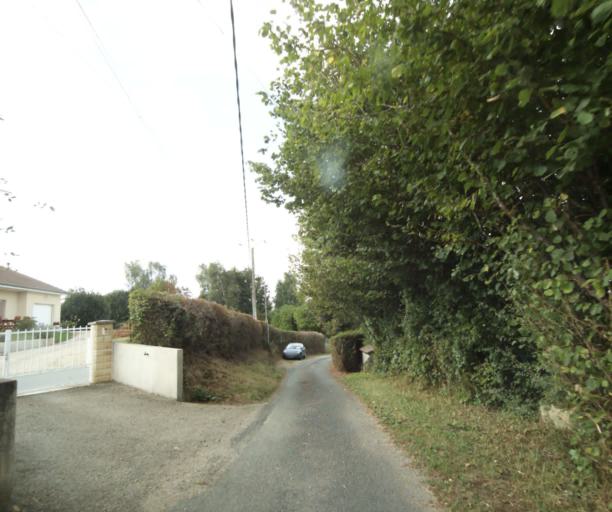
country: FR
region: Bourgogne
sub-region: Departement de Saone-et-Loire
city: Palinges
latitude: 46.4903
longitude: 4.2109
